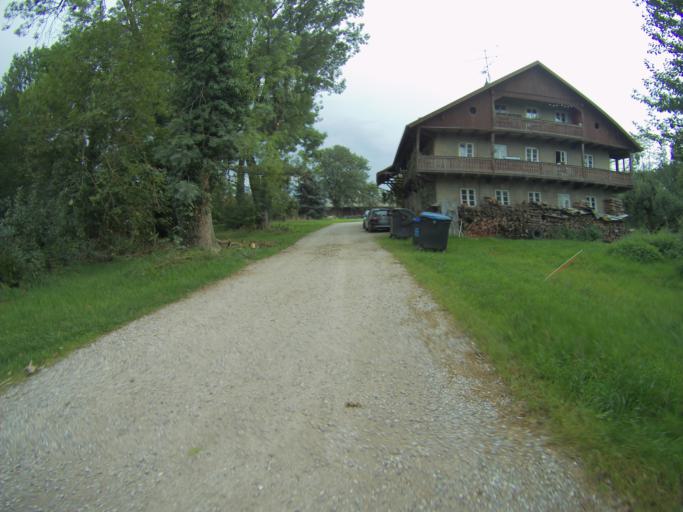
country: DE
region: Bavaria
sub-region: Upper Bavaria
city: Marzling
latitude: 48.3841
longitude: 11.8346
